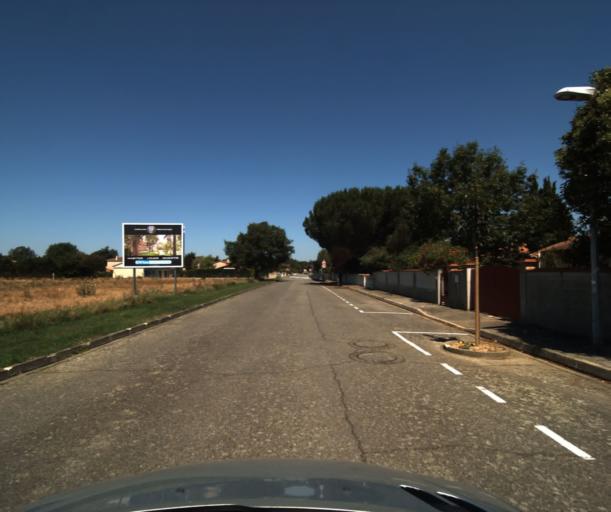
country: FR
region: Midi-Pyrenees
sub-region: Departement de la Haute-Garonne
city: Roquettes
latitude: 43.4941
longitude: 1.3615
